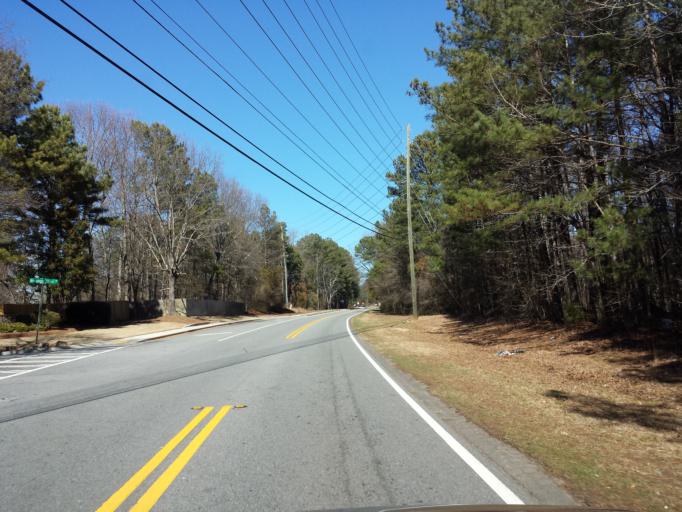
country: US
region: Georgia
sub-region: Cobb County
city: Marietta
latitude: 33.9287
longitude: -84.6156
